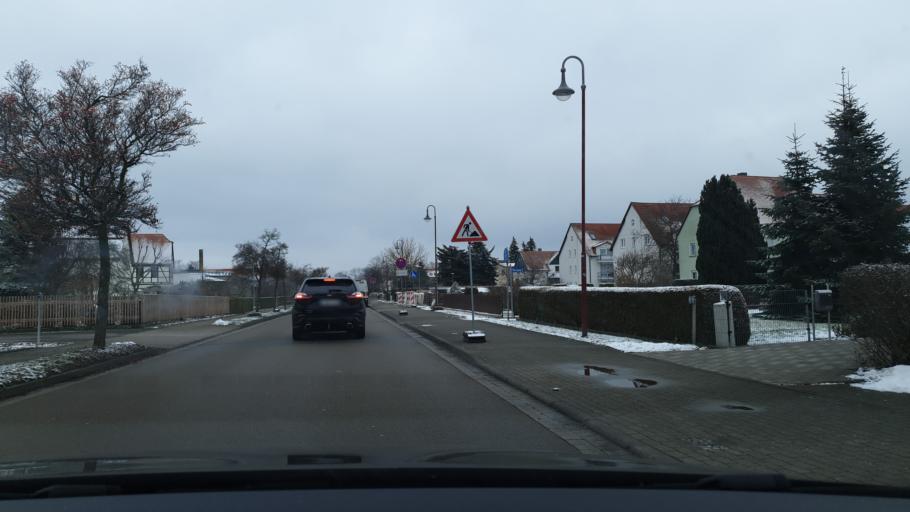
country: DE
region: Saxony
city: Grossposna
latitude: 51.2933
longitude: 12.5176
